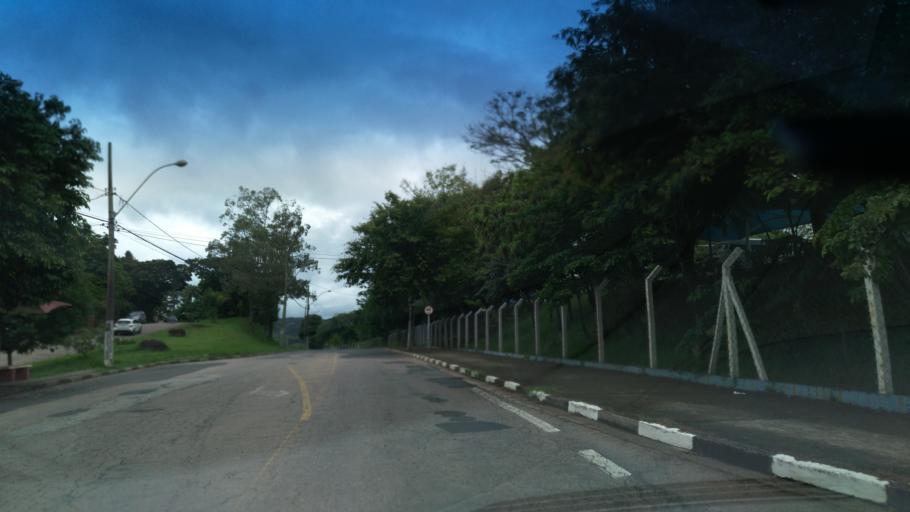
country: BR
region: Sao Paulo
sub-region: Valinhos
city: Valinhos
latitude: -22.9698
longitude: -46.9836
